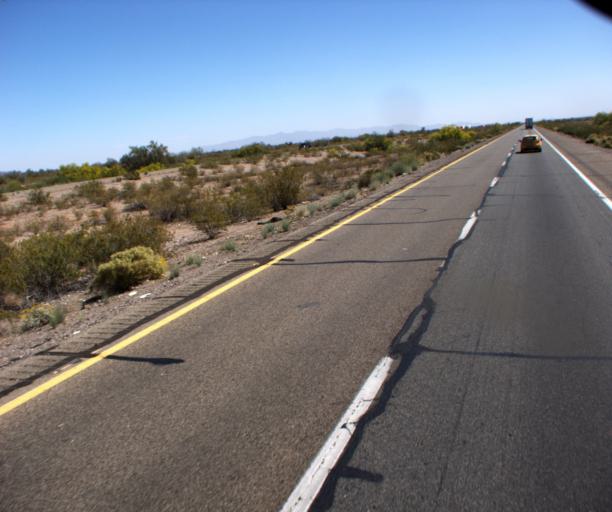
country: US
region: Arizona
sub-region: Maricopa County
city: Buckeye
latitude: 33.5088
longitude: -113.0019
